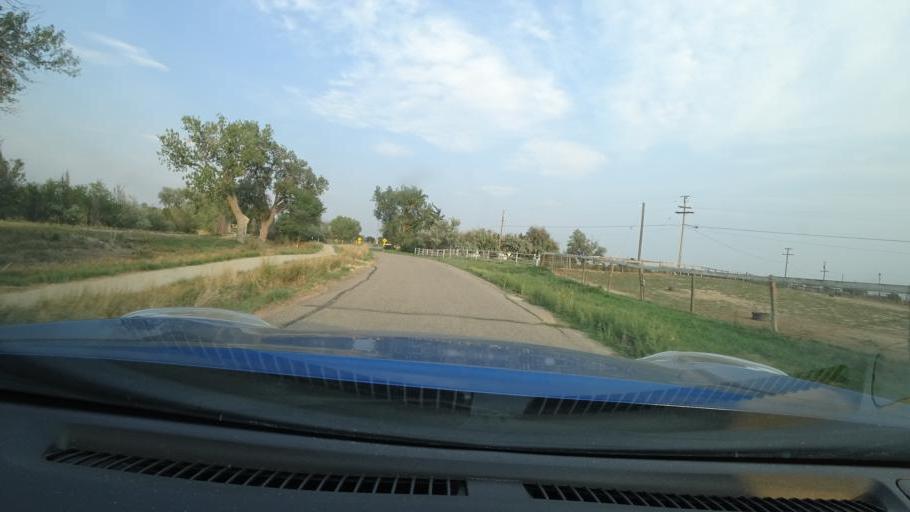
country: US
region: Colorado
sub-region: Adams County
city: Aurora
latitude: 39.7369
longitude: -104.7834
